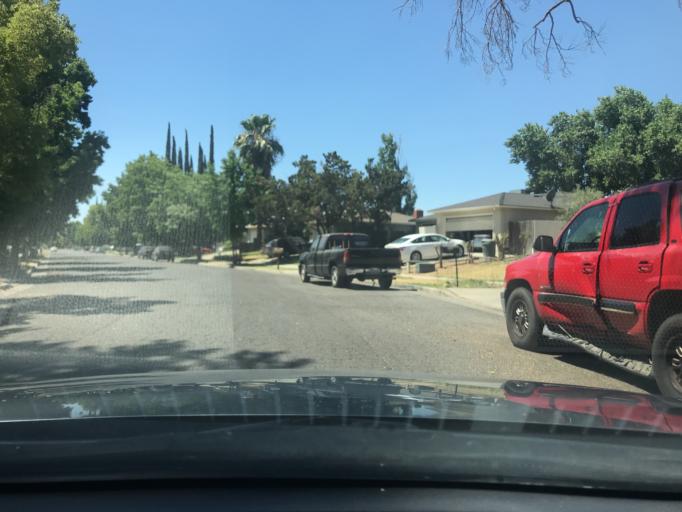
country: US
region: California
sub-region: Merced County
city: Merced
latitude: 37.3233
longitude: -120.5009
